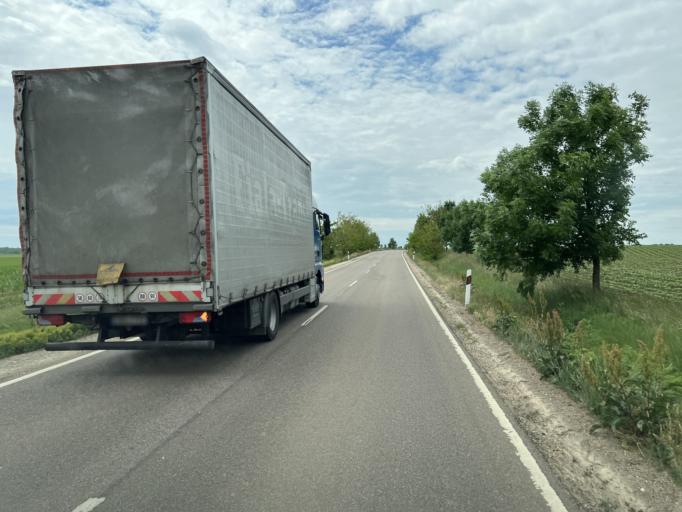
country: HU
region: Pest
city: Zsambok
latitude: 47.5151
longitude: 19.5988
